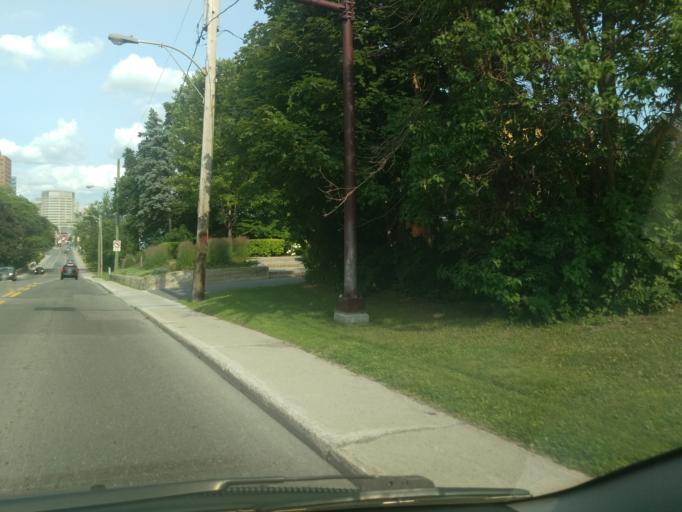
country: CA
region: Ontario
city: Ottawa
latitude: 45.4240
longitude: -75.7278
